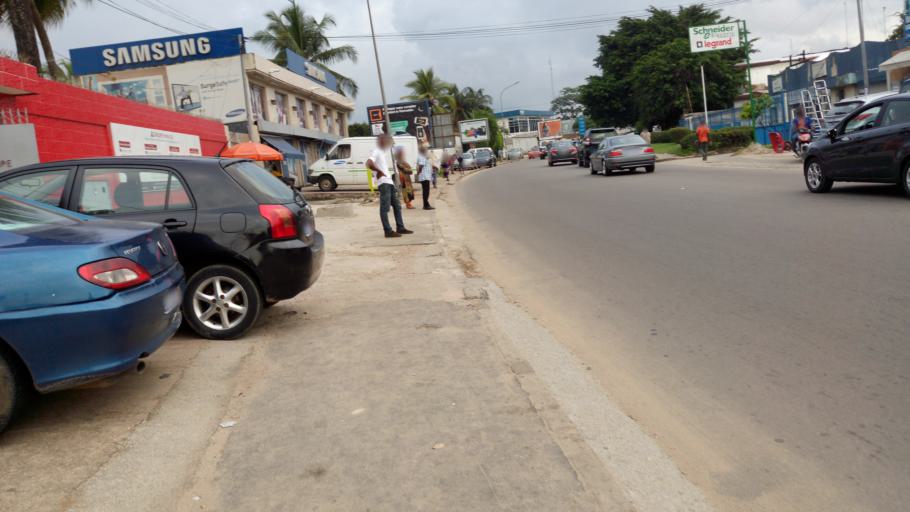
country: CI
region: Lagunes
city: Abidjan
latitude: 5.3561
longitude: -3.9919
